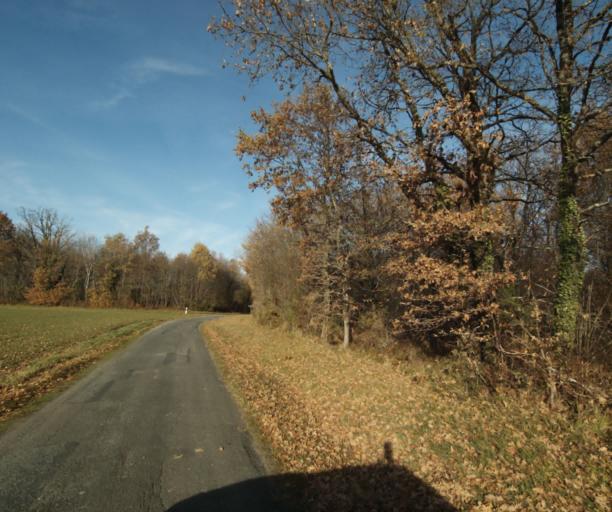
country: FR
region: Poitou-Charentes
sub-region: Departement de la Charente-Maritime
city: Burie
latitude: 45.7535
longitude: -0.4900
